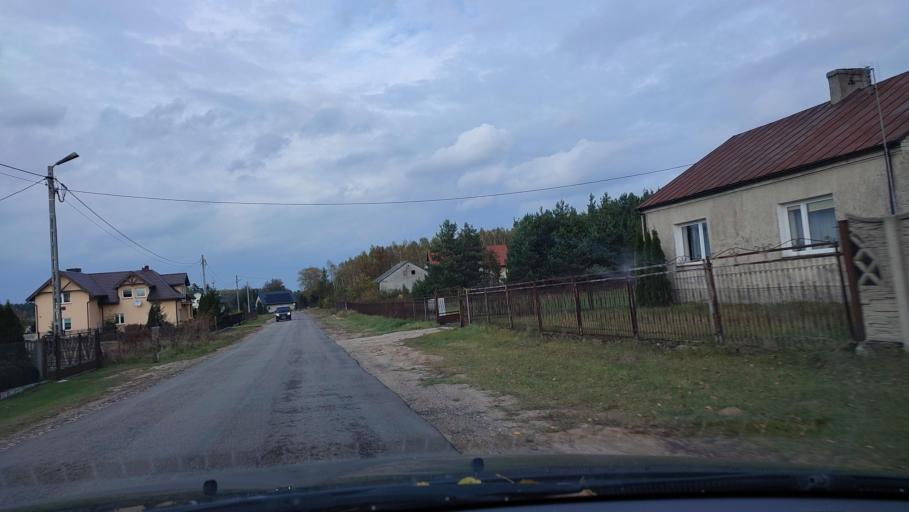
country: PL
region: Masovian Voivodeship
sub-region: Powiat mlawski
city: Mlawa
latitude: 53.1668
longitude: 20.3641
